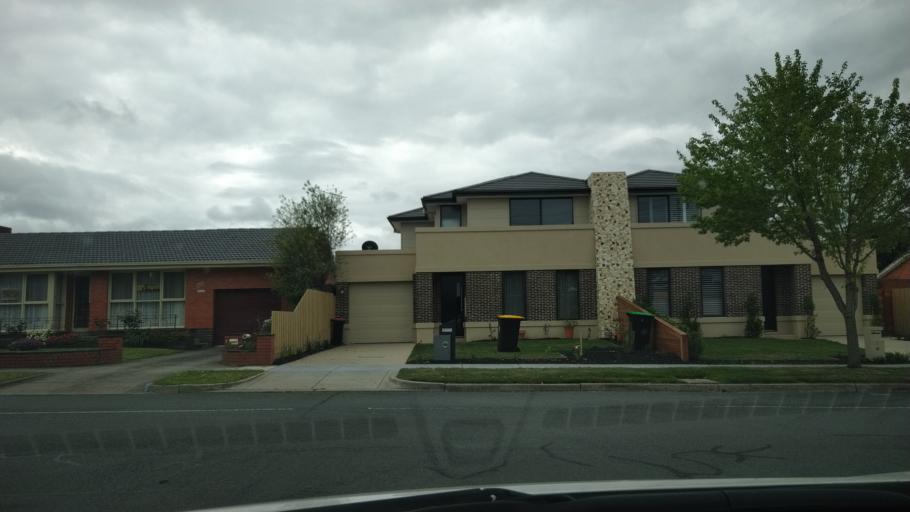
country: AU
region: Victoria
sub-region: Kingston
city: Mentone
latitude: -37.9674
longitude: 145.0778
